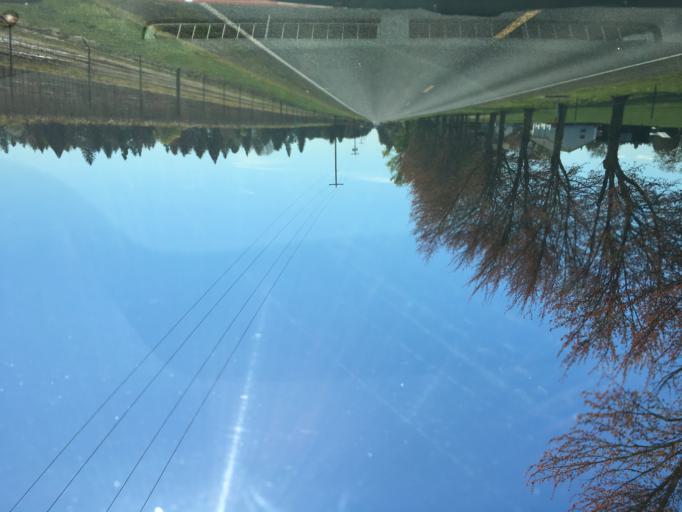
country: US
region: Oregon
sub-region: Clackamas County
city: Canby
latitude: 45.2279
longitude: -122.7228
